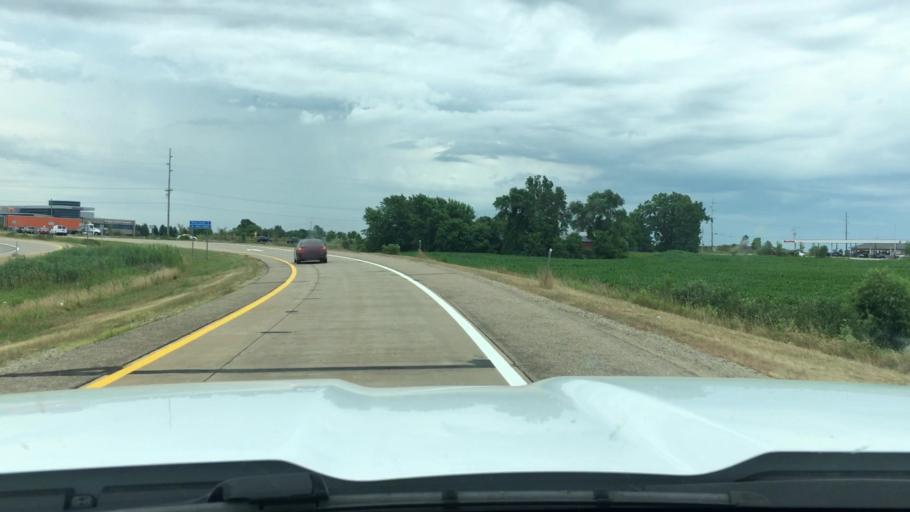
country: US
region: Michigan
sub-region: Kent County
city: Byron Center
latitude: 42.8515
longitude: -85.7257
